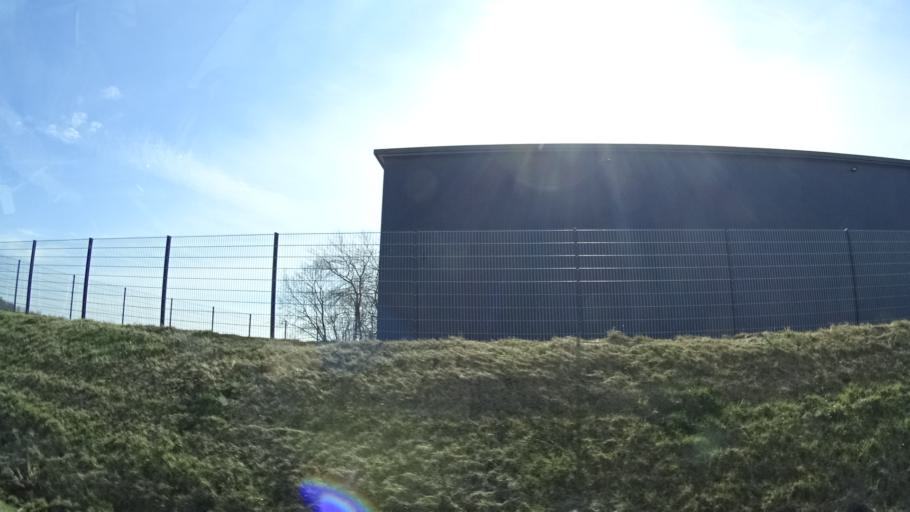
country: DE
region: Hesse
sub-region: Regierungsbezirk Giessen
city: Grunberg
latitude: 50.6090
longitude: 8.9574
